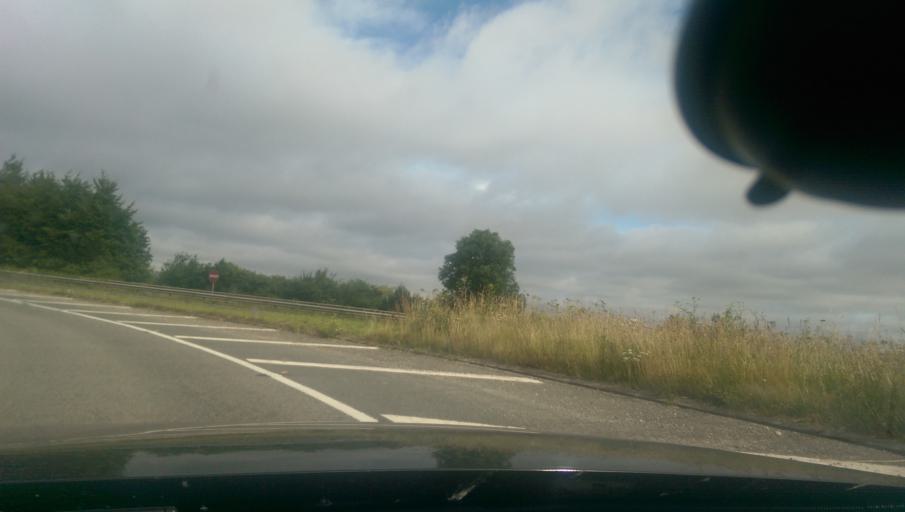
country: GB
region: England
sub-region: Hampshire
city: Andover
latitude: 51.2001
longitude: -1.4473
